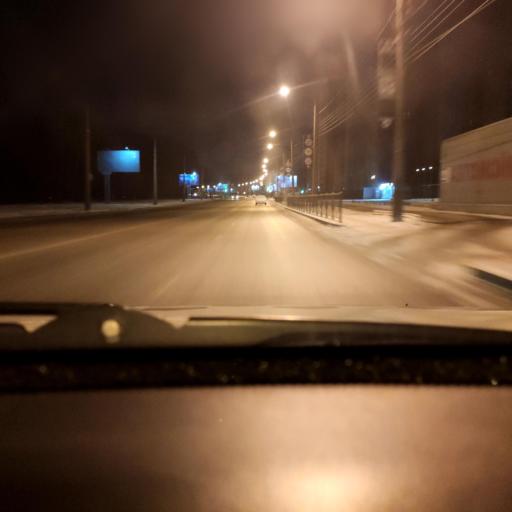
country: RU
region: Perm
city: Kondratovo
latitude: 57.9795
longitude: 56.1705
